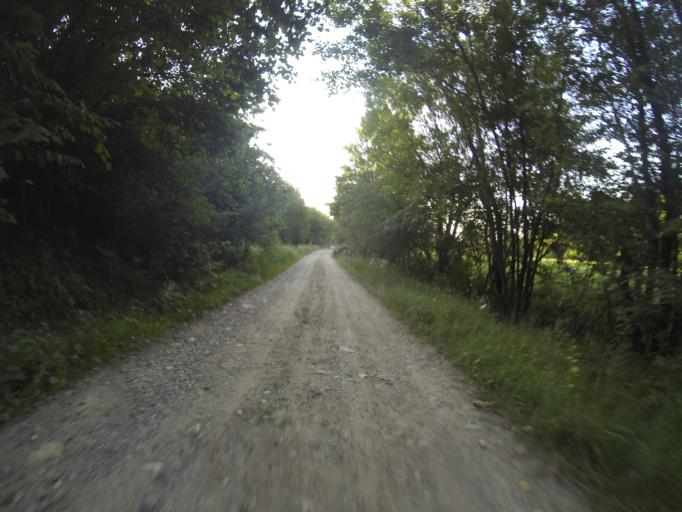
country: RO
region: Brasov
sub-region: Comuna Sinca Veche
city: Sinca Veche
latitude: 45.7414
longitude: 25.1949
